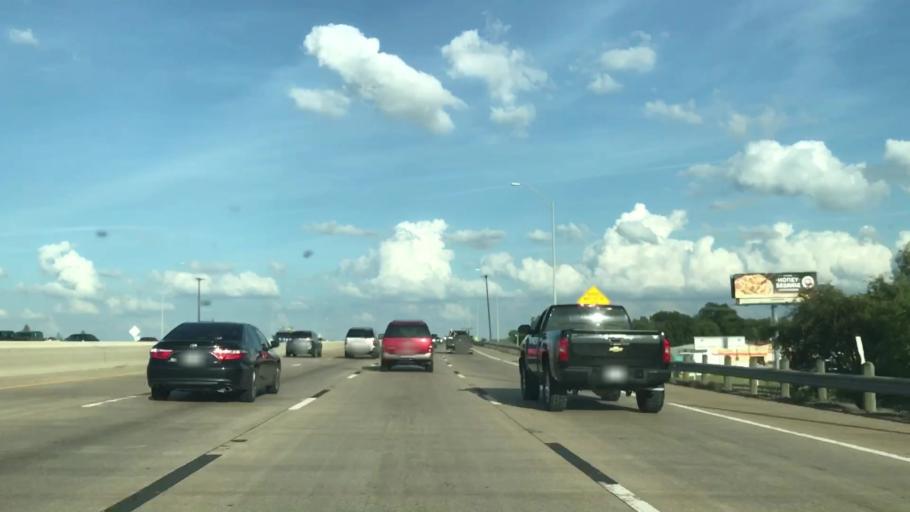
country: US
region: Texas
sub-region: Dallas County
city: Grand Prairie
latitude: 32.7620
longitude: -96.9622
